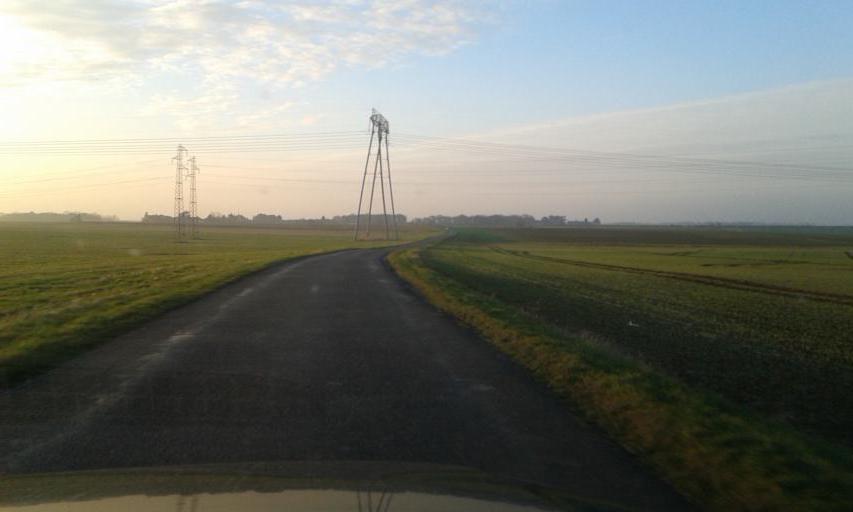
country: FR
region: Centre
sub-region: Departement du Loiret
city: Tavers
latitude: 47.7695
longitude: 1.5638
